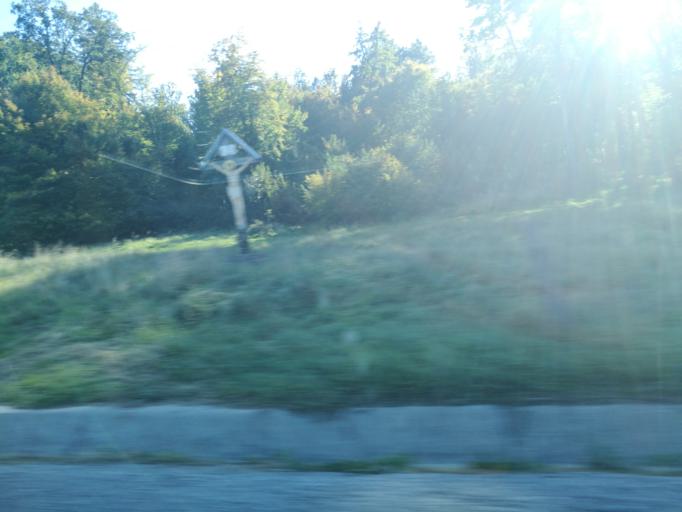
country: RO
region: Brasov
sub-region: Comuna Dumbravita
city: Dumbravita
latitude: 45.7625
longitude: 25.3806
